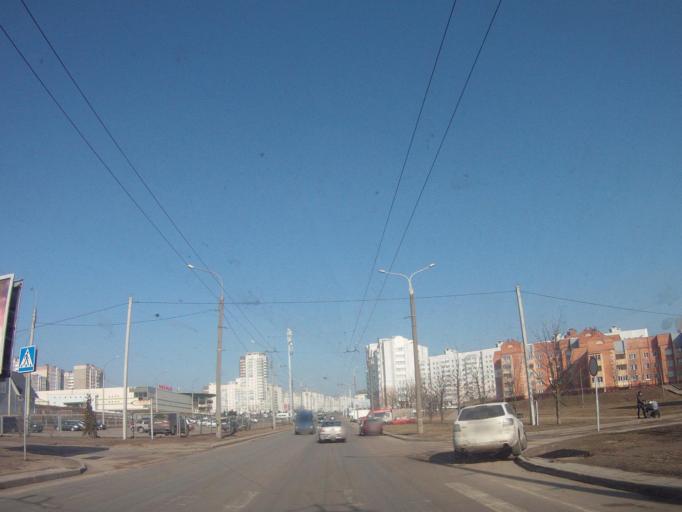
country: BY
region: Minsk
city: Novoye Medvezhino
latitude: 53.8849
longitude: 27.4302
